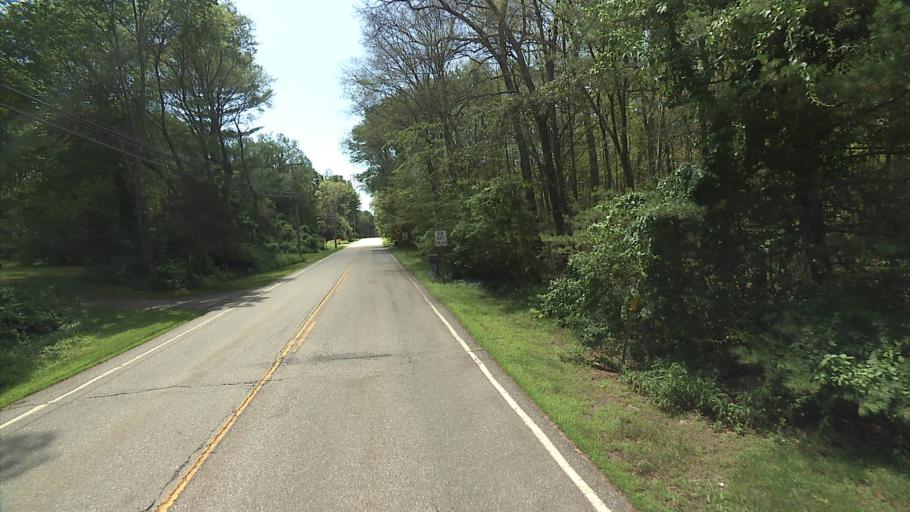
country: US
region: Connecticut
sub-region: Middlesex County
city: East Hampton
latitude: 41.5555
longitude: -72.5107
